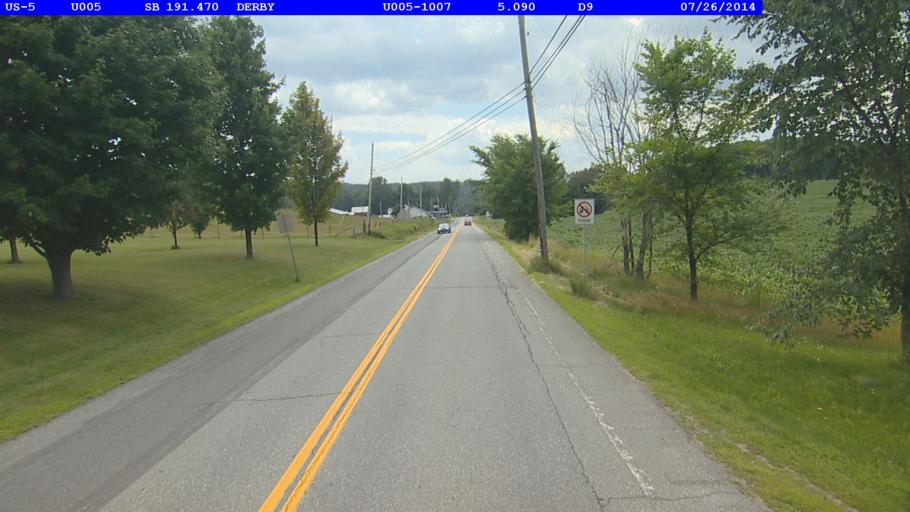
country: US
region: Vermont
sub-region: Orleans County
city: Newport
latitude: 44.9947
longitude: -72.1063
